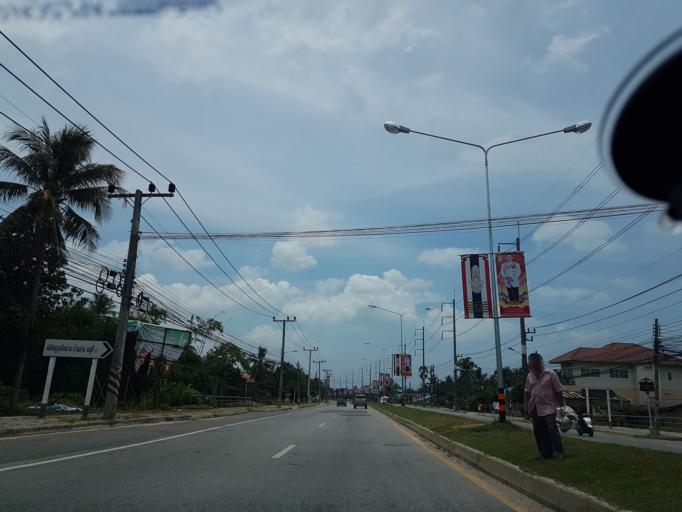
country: TH
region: Songkhla
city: Songkhla
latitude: 7.1123
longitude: 100.6326
